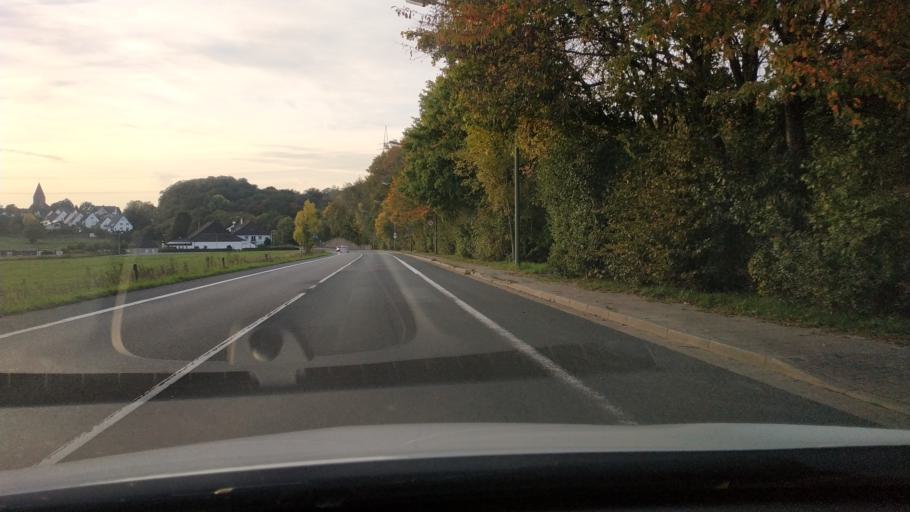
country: DE
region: Lower Saxony
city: Bissendorf
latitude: 52.2476
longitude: 8.1198
